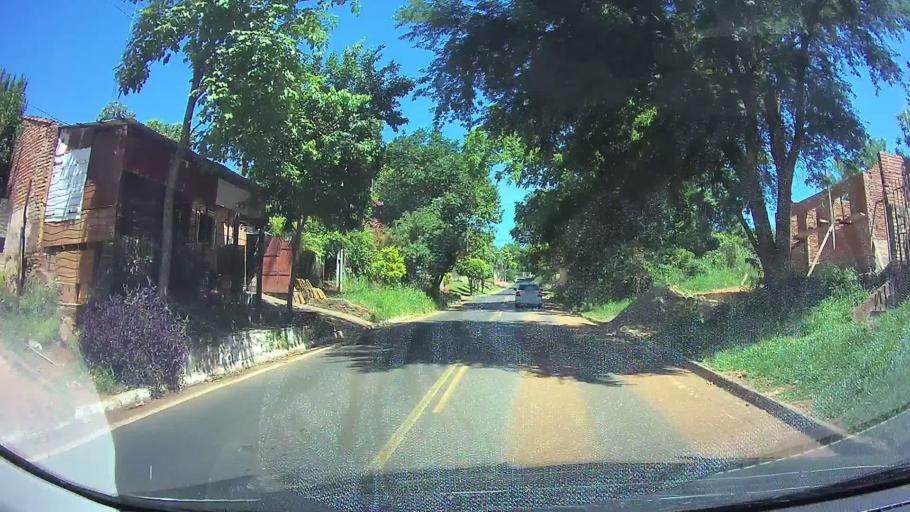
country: PY
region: Central
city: Aregua
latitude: -25.3178
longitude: -57.3904
